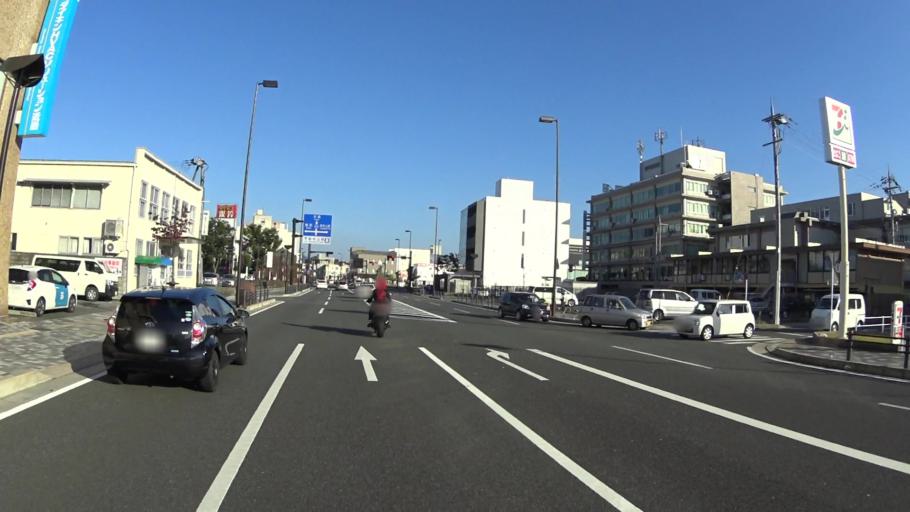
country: JP
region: Kyoto
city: Fukuchiyama
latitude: 35.2995
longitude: 135.1180
